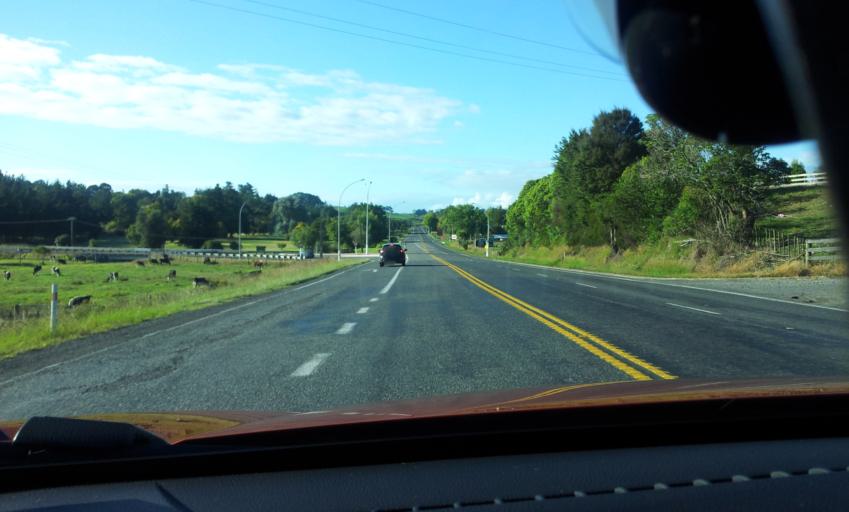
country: NZ
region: Waikato
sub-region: Hauraki District
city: Ngatea
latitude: -37.2899
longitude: 175.3708
